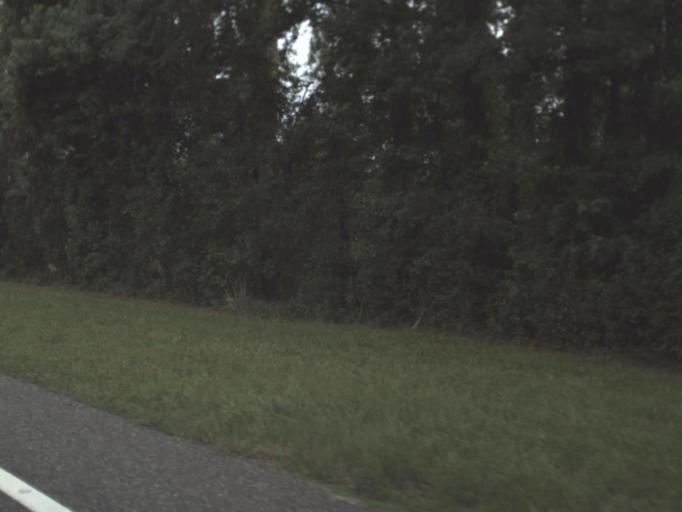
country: US
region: Florida
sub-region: Levy County
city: Bronson
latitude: 29.2819
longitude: -82.7411
